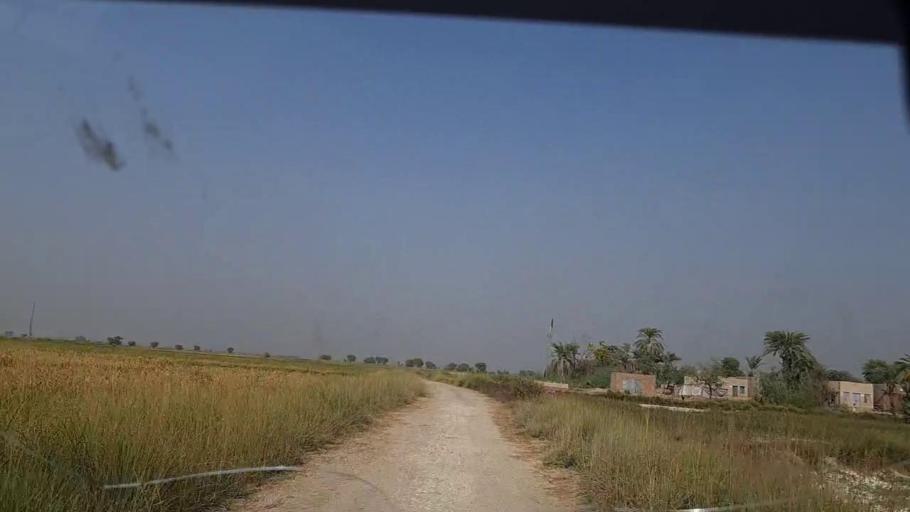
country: PK
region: Sindh
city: Shikarpur
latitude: 28.0943
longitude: 68.6003
